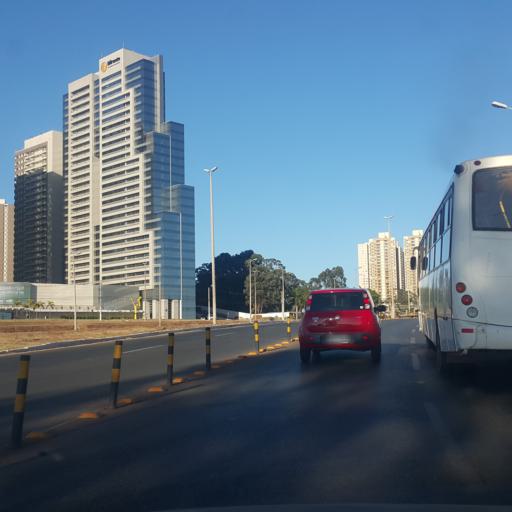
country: BR
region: Federal District
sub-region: Brasilia
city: Brasilia
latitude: -15.8301
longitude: -48.0404
